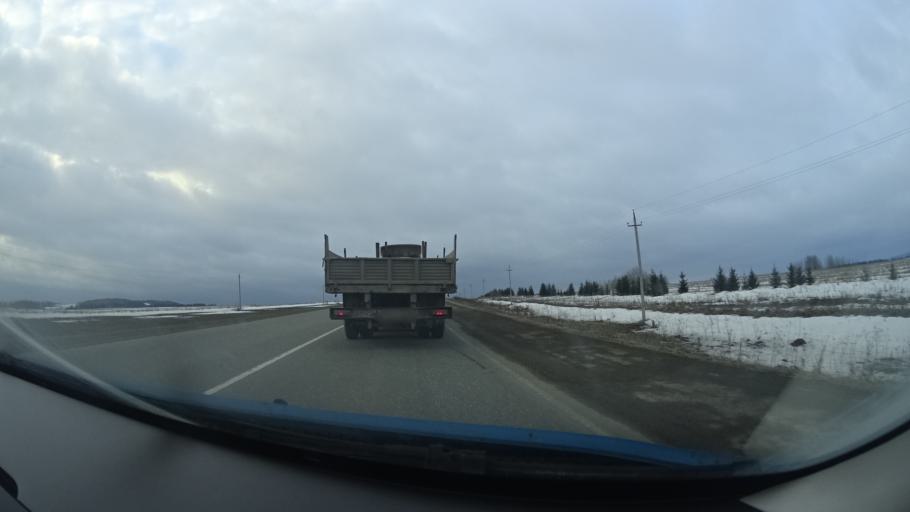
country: RU
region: Perm
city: Osa
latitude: 57.2500
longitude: 55.5881
